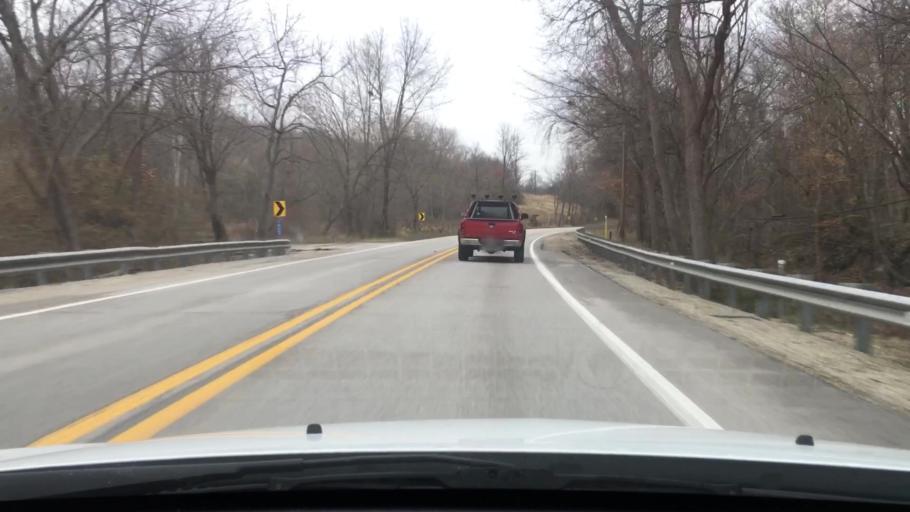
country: US
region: Missouri
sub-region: Pike County
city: Louisiana
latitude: 39.5182
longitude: -90.9549
